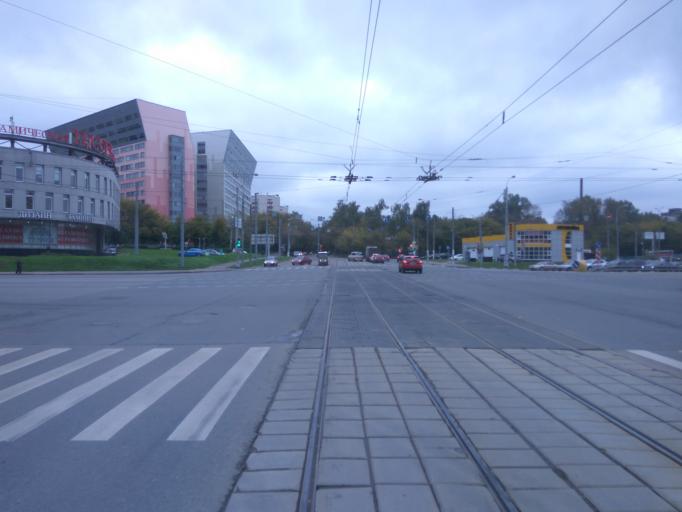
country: RU
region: Moscow
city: Kotlovka
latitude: 55.6632
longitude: 37.6131
